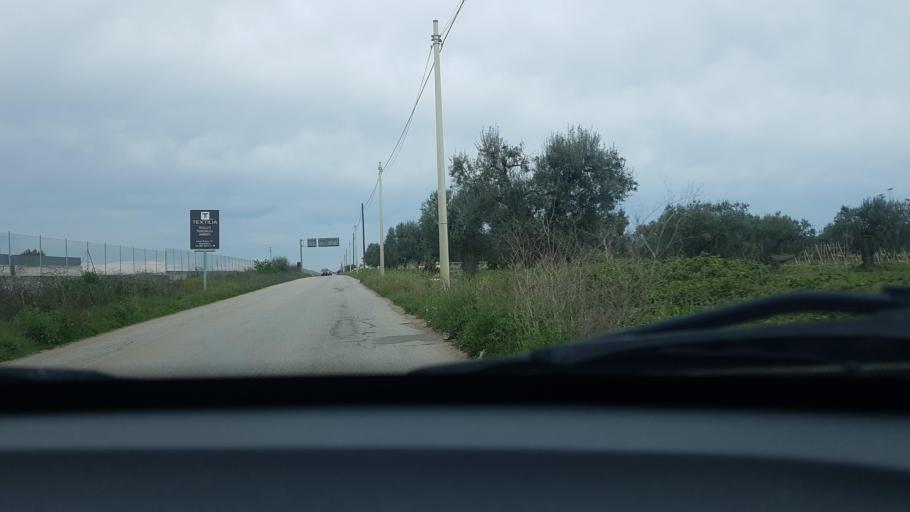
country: IT
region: Apulia
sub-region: Provincia di Bari
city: Noicattaro
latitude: 41.0337
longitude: 16.9772
